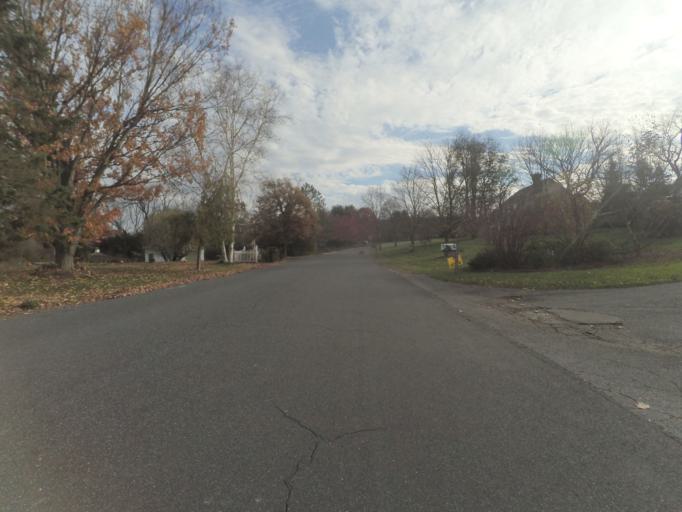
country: US
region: Pennsylvania
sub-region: Centre County
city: Boalsburg
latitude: 40.7775
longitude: -77.8127
